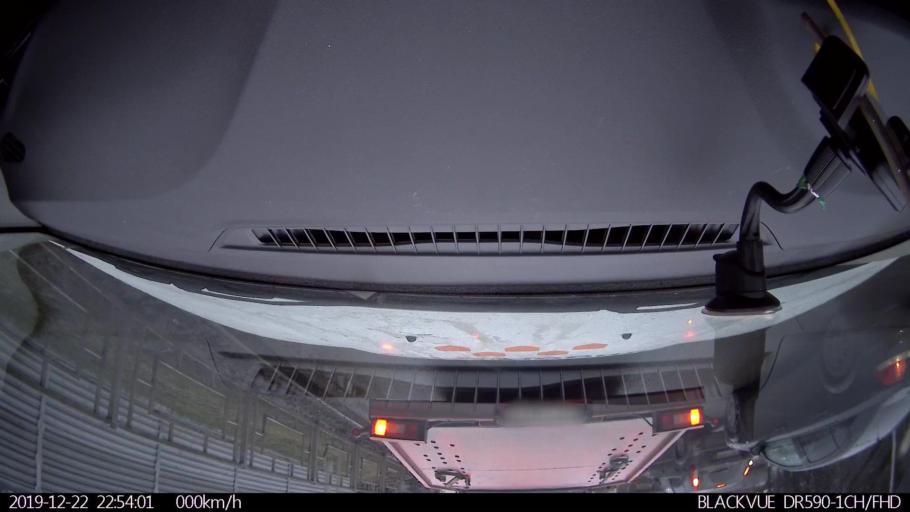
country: RU
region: Nizjnij Novgorod
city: Gorbatovka
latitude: 56.2429
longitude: 43.8509
